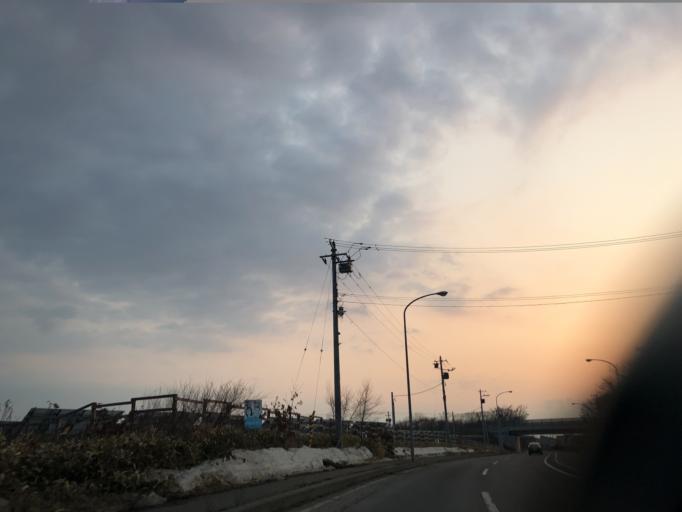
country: JP
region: Hokkaido
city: Chitose
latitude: 42.8324
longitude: 141.6931
